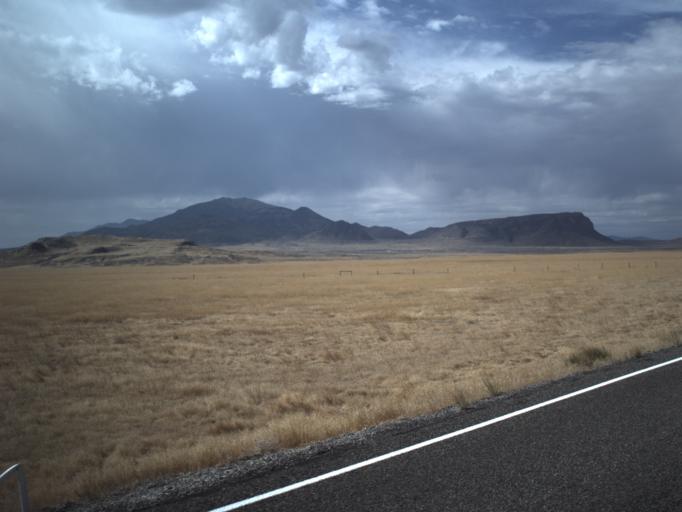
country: US
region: Utah
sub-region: Tooele County
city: Wendover
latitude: 41.3932
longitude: -113.9673
